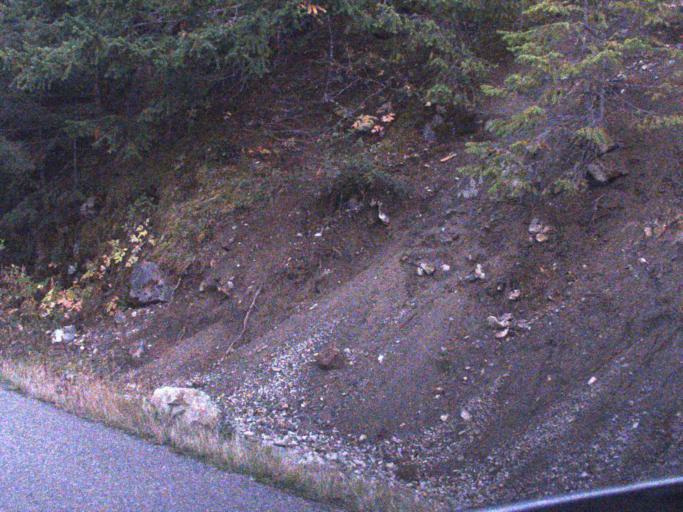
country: US
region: Washington
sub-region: Snohomish County
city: Darrington
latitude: 48.7129
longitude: -120.9940
